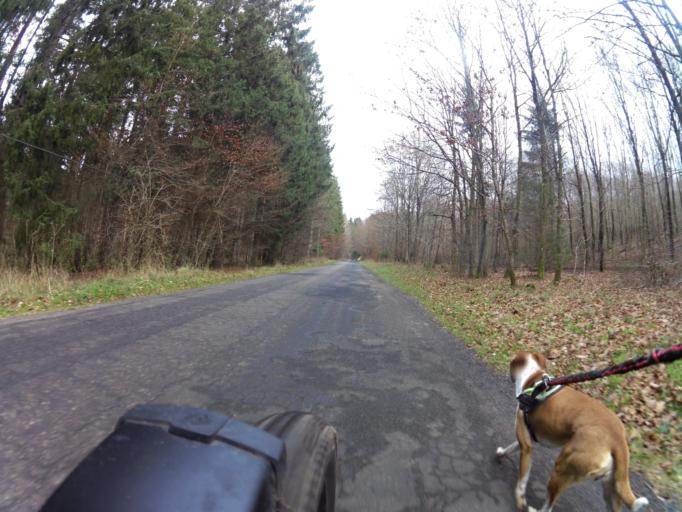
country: PL
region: West Pomeranian Voivodeship
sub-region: Powiat koszalinski
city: Polanow
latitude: 54.0749
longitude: 16.6577
